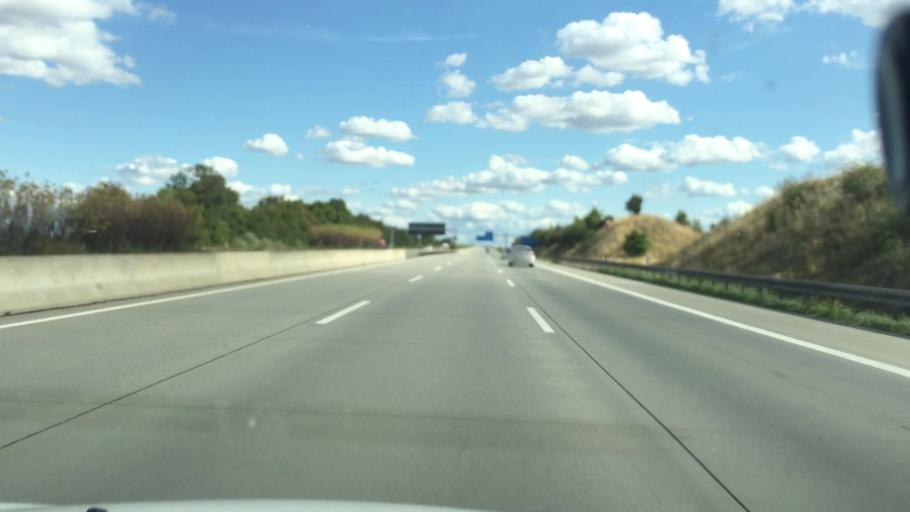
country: DE
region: Thuringia
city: Schwaara
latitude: 50.8968
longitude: 12.1373
